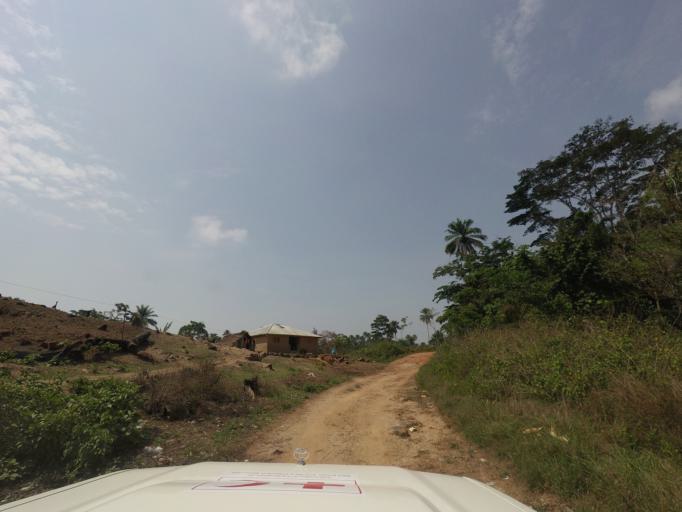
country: LR
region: Lofa
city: Voinjama
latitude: 8.5142
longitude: -9.6291
